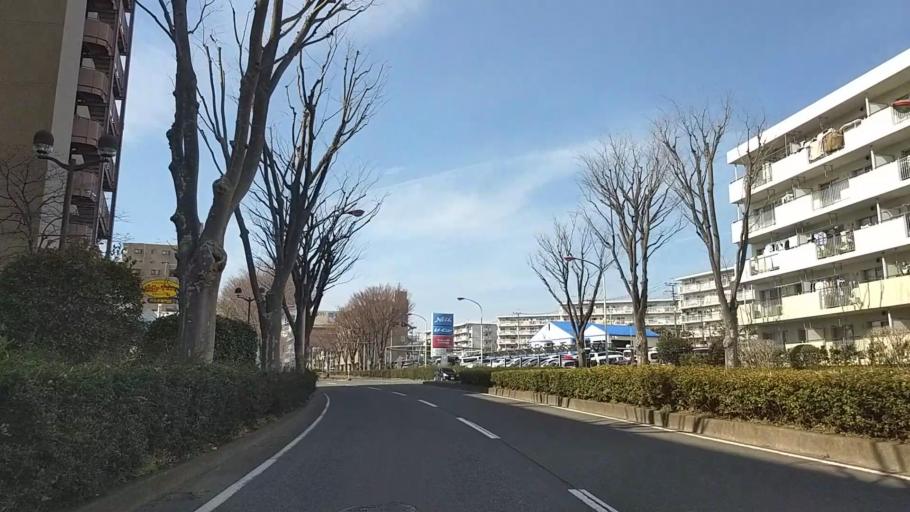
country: JP
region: Kanagawa
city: Fujisawa
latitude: 35.3692
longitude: 139.4461
